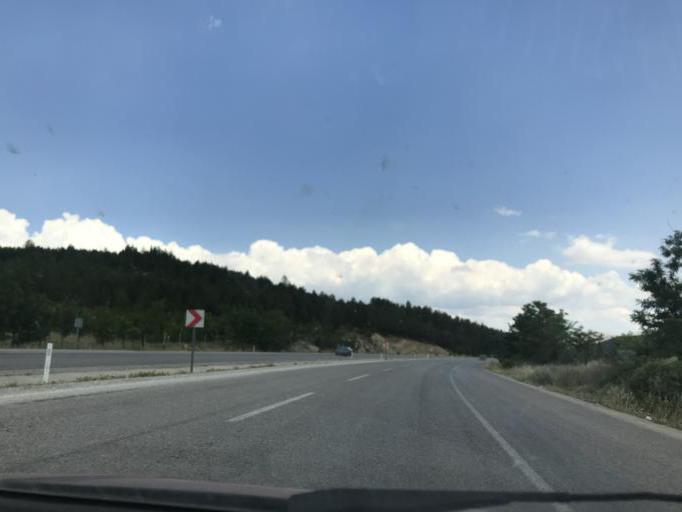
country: TR
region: Denizli
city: Tavas
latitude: 37.6141
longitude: 29.1452
